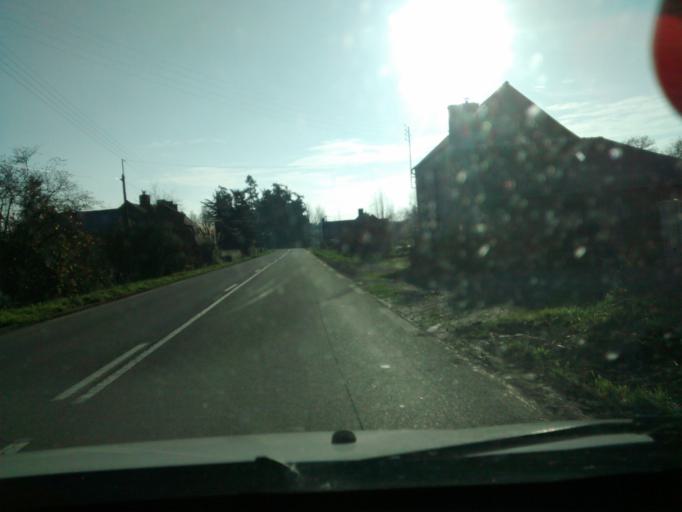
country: FR
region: Brittany
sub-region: Departement d'Ille-et-Vilaine
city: Tremblay
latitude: 48.4000
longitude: -1.4847
